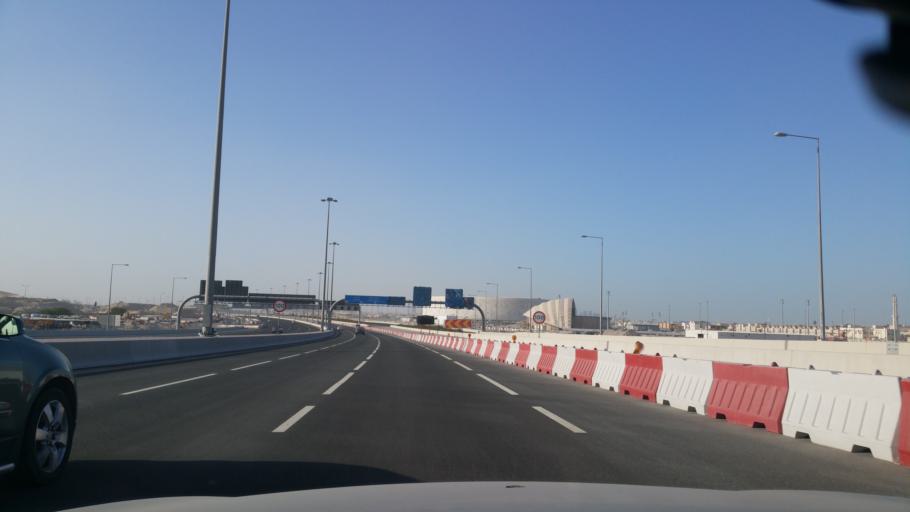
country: QA
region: Baladiyat ad Dawhah
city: Doha
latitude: 25.2246
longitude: 51.5336
